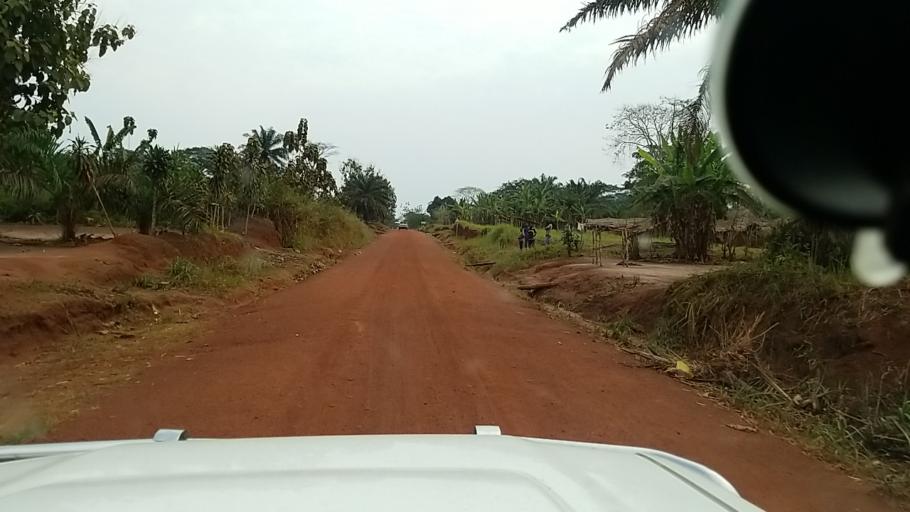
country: CD
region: Equateur
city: Gemena
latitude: 2.9696
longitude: 19.9001
